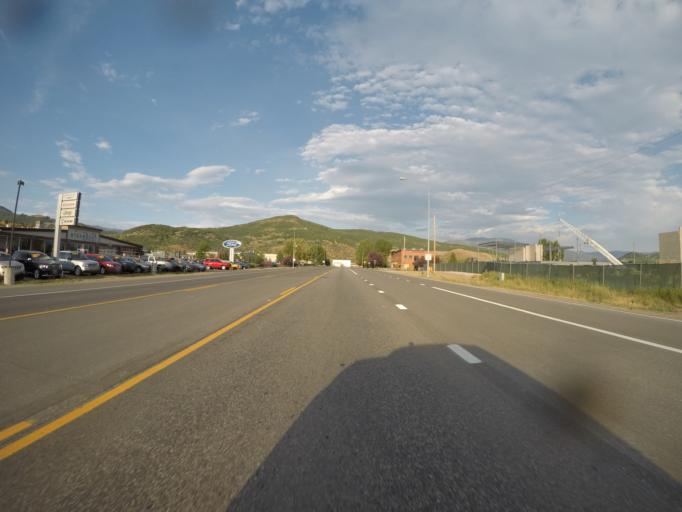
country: US
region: Colorado
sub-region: Routt County
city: Steamboat Springs
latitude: 40.5029
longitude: -106.8611
